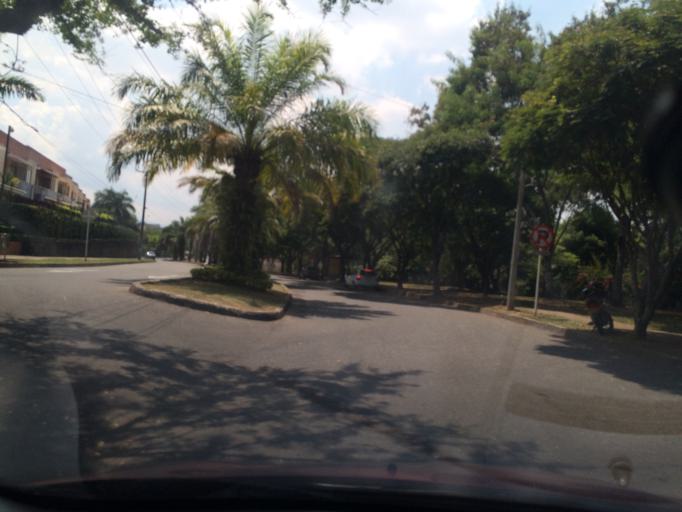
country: CO
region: Valle del Cauca
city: Cali
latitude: 3.3631
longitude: -76.5374
